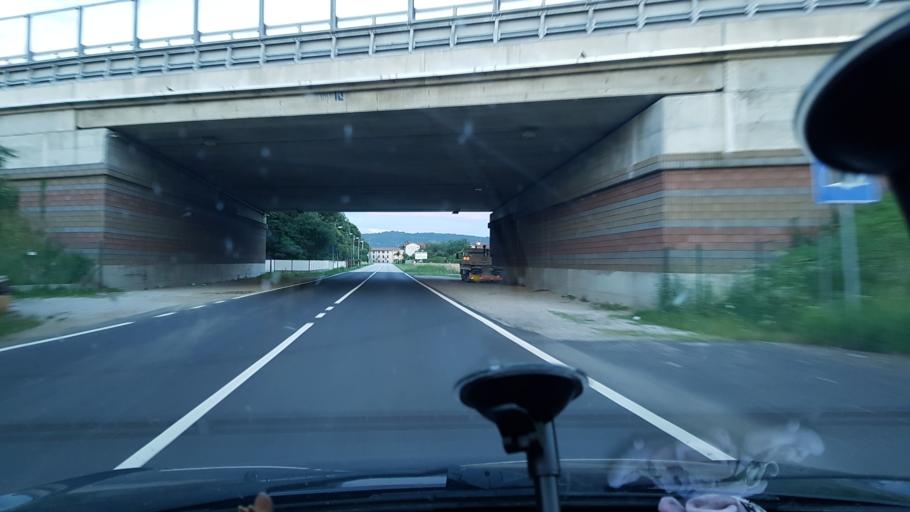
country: IT
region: Friuli Venezia Giulia
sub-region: Provincia di Gorizia
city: Sagrado
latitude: 45.8932
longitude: 13.4728
